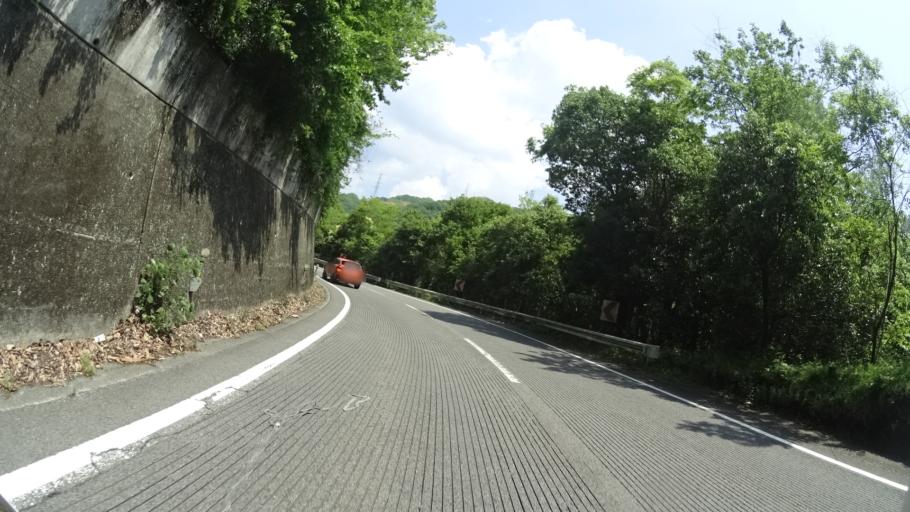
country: JP
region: Ehime
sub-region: Shikoku-chuo Shi
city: Matsuyama
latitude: 33.8754
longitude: 132.8342
